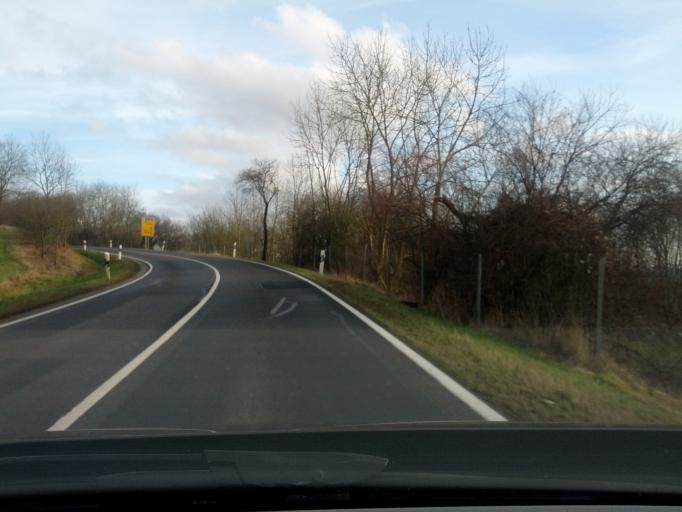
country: DE
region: Thuringia
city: Ifta
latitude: 51.0540
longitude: 10.2072
